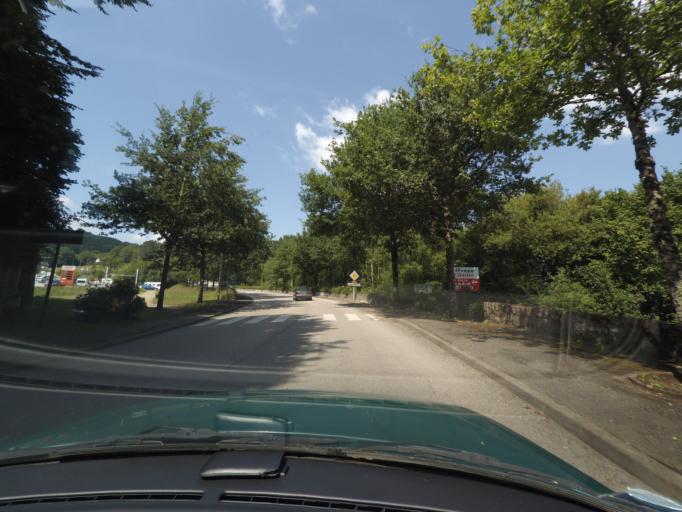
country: FR
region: Limousin
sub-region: Departement de la Haute-Vienne
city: Eymoutiers
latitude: 45.7386
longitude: 1.7360
